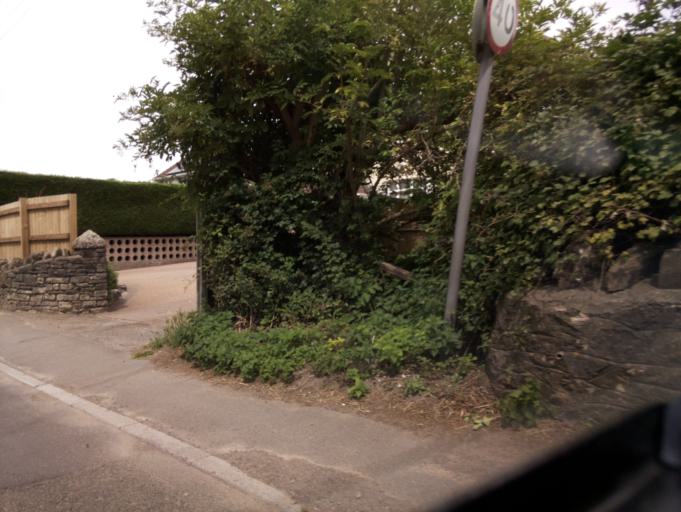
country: GB
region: England
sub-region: North Somerset
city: Yatton
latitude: 51.3990
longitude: -2.8368
